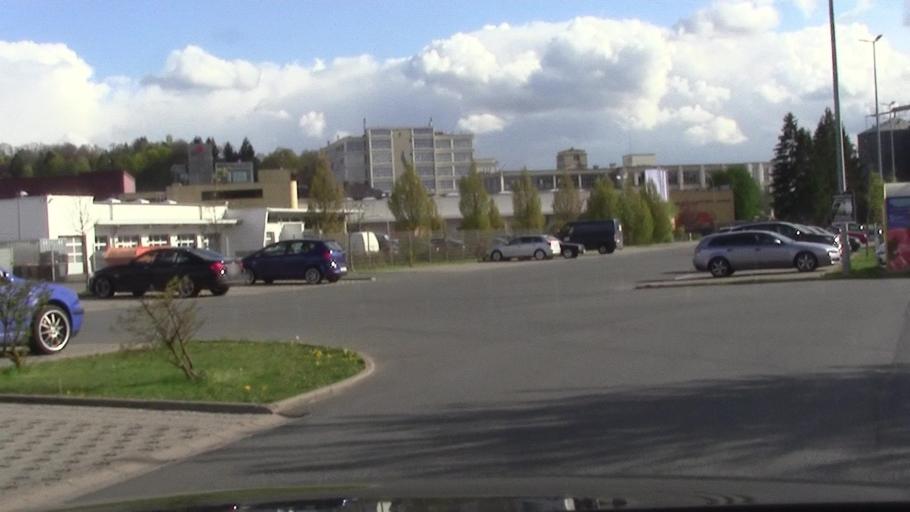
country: DE
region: Bavaria
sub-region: Upper Franconia
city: Kulmbach
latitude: 50.1122
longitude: 11.4515
